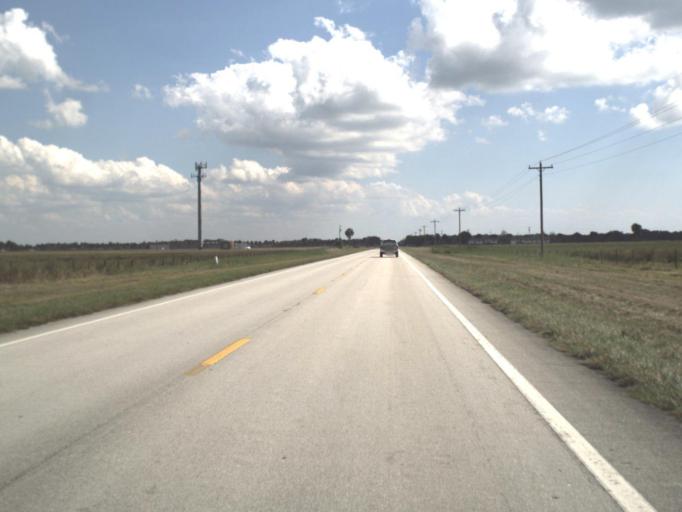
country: US
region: Florida
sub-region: Okeechobee County
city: Okeechobee
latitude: 27.3358
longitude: -80.9348
